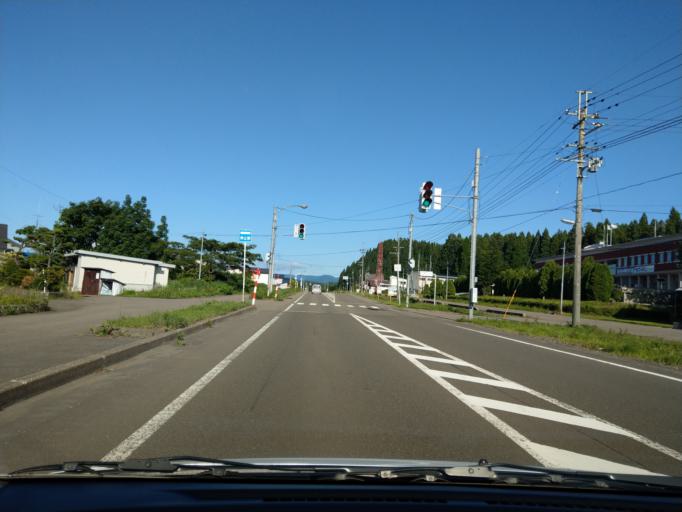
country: JP
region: Akita
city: Takanosu
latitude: 40.1194
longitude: 140.3805
